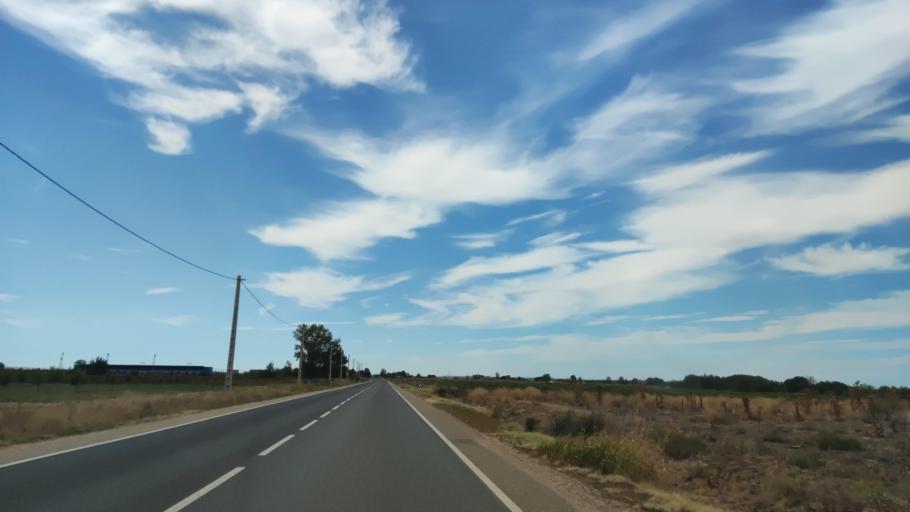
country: ES
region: Castille and Leon
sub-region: Provincia de Zamora
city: Madridanos
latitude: 41.4916
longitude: -5.6335
